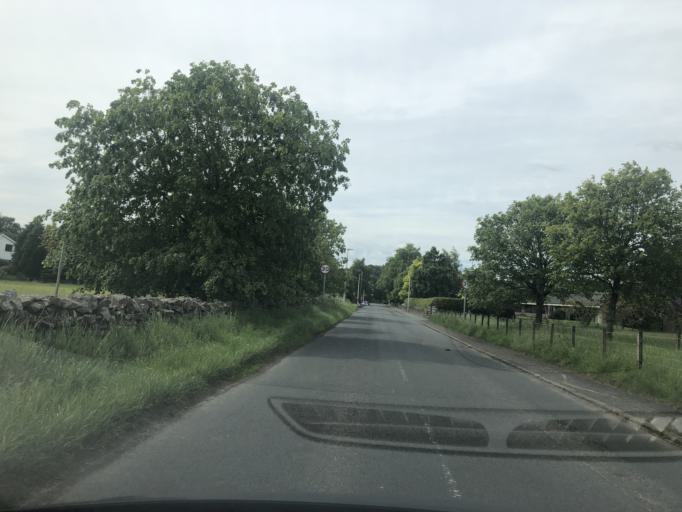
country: GB
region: Scotland
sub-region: The Scottish Borders
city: West Linton
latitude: 55.7469
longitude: -3.3517
